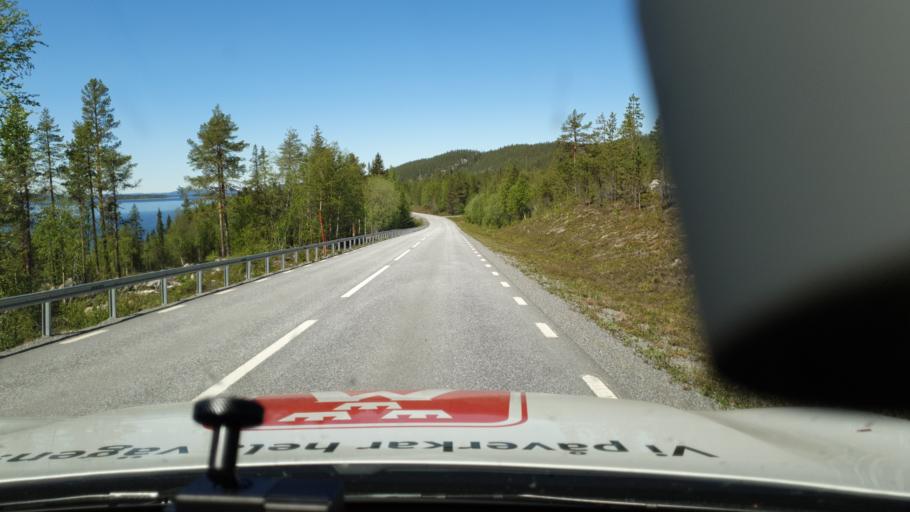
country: SE
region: Vaesterbotten
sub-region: Storumans Kommun
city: Storuman
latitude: 65.1486
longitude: 17.0742
